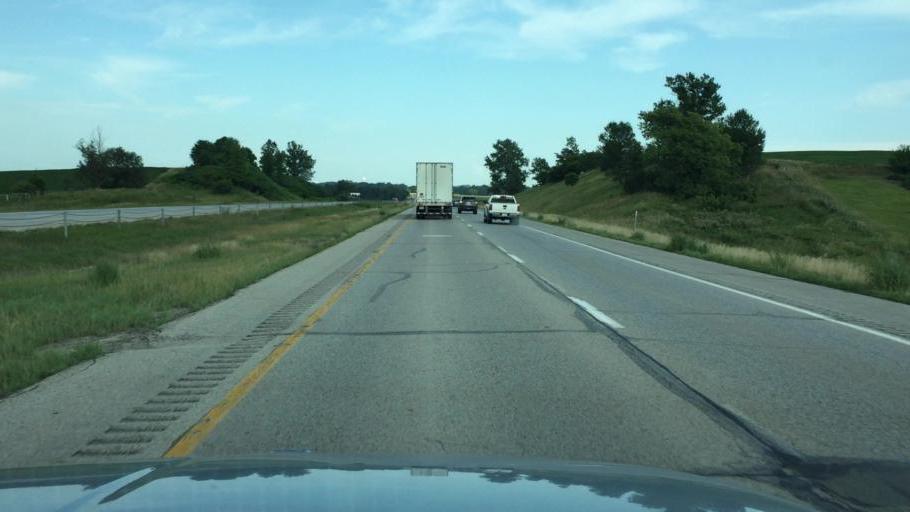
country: US
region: Iowa
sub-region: Johnson County
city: Tiffin
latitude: 41.6951
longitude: -91.7115
